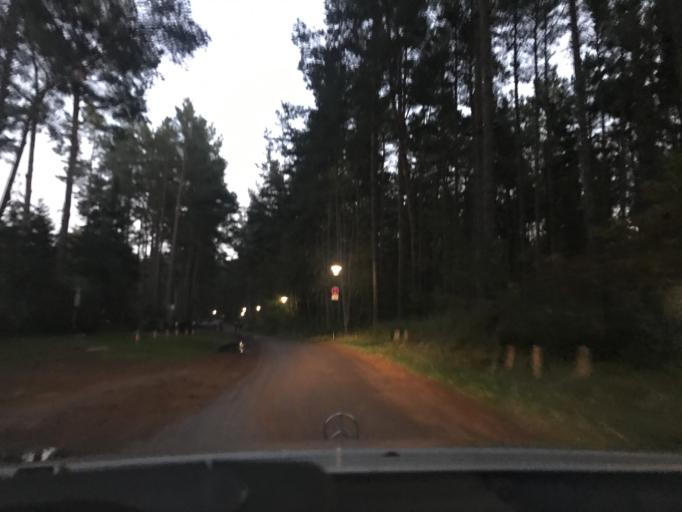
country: DE
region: Mecklenburg-Vorpommern
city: Karlshagen
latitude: 54.1133
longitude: 13.8506
